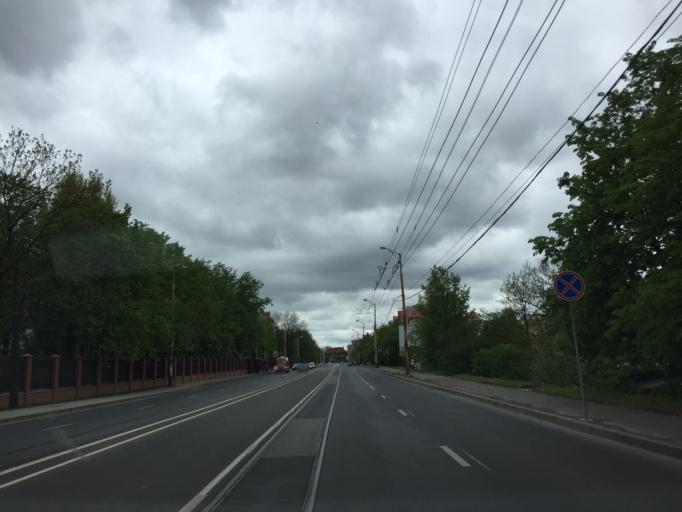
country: RU
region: Kaliningrad
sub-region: Gorod Kaliningrad
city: Kaliningrad
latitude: 54.6940
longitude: 20.4781
